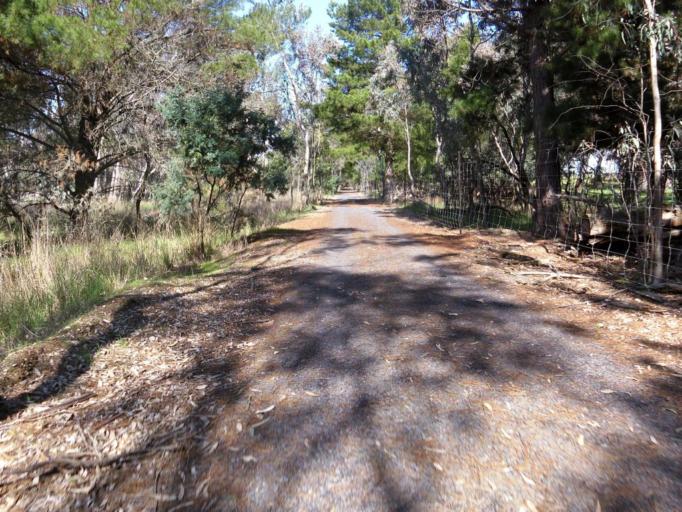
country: AU
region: Victoria
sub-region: Murrindindi
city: Alexandra
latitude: -36.9963
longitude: 145.7419
